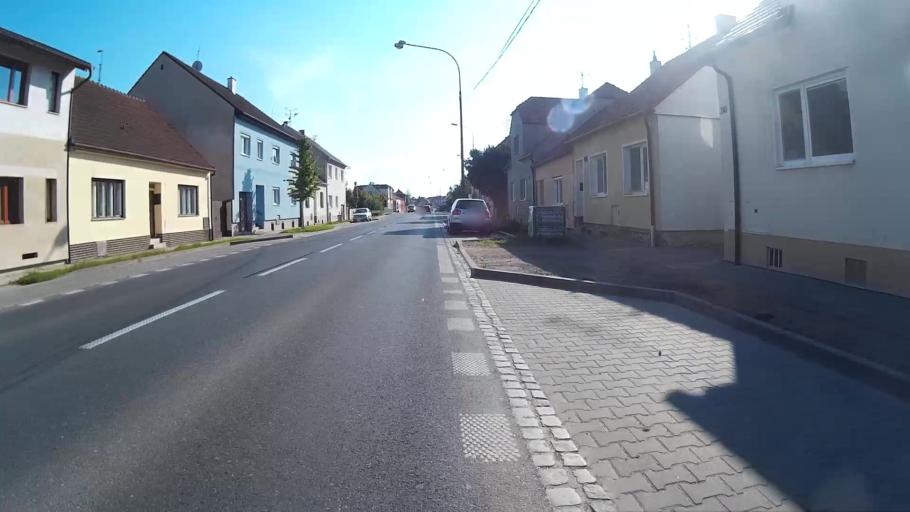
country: CZ
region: South Moravian
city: Pohorelice
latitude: 48.9852
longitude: 16.5306
